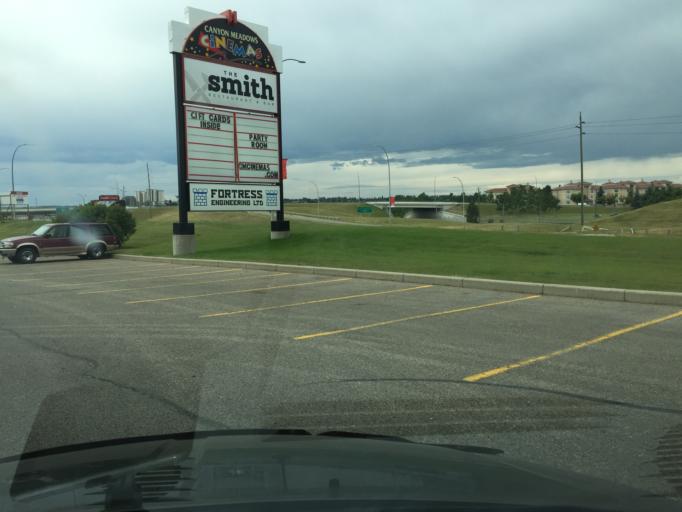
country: CA
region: Alberta
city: Calgary
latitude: 50.9341
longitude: -114.0675
